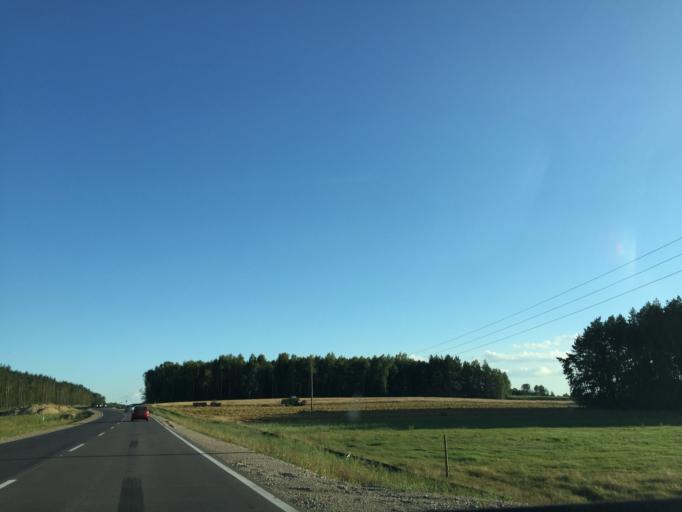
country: PL
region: Podlasie
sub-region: Powiat kolnenski
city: Stawiski
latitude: 53.3375
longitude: 22.1553
